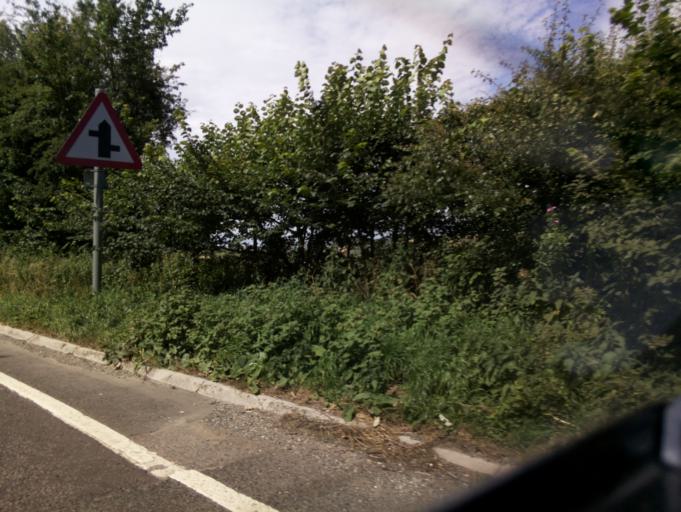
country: GB
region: England
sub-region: Dorset
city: Dorchester
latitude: 50.7582
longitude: -2.5238
